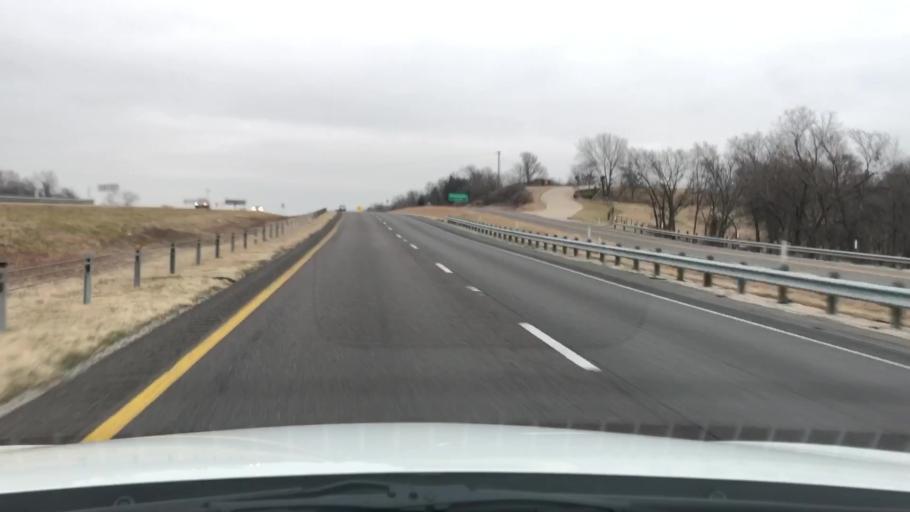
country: US
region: Texas
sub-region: Cooke County
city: Gainesville
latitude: 33.7079
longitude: -97.1619
